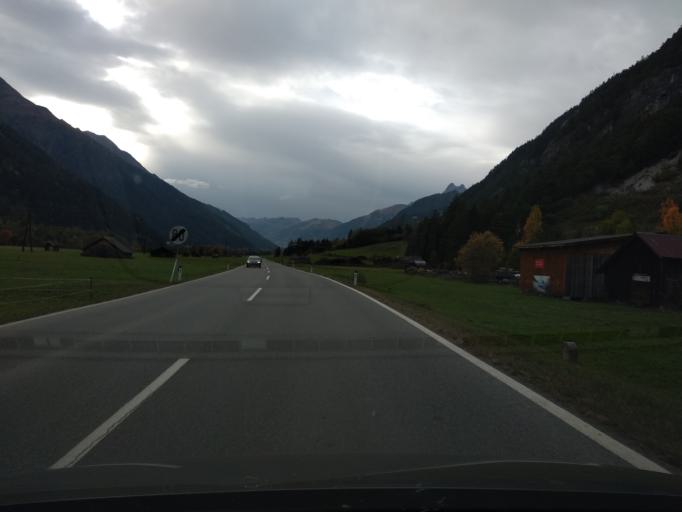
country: AT
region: Tyrol
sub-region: Politischer Bezirk Landeck
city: Flirsch
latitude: 47.1530
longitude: 10.3724
